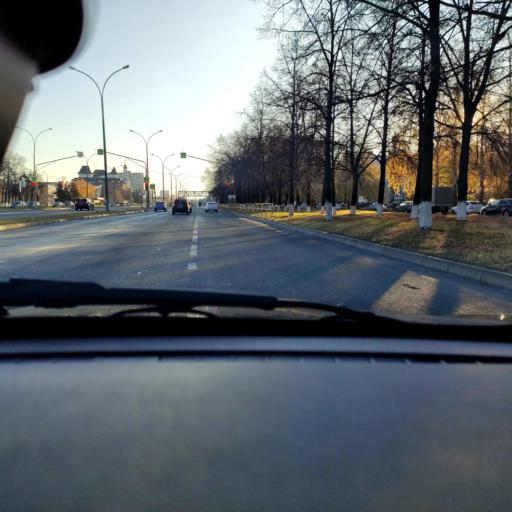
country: RU
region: Samara
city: Tol'yatti
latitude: 53.5297
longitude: 49.2709
